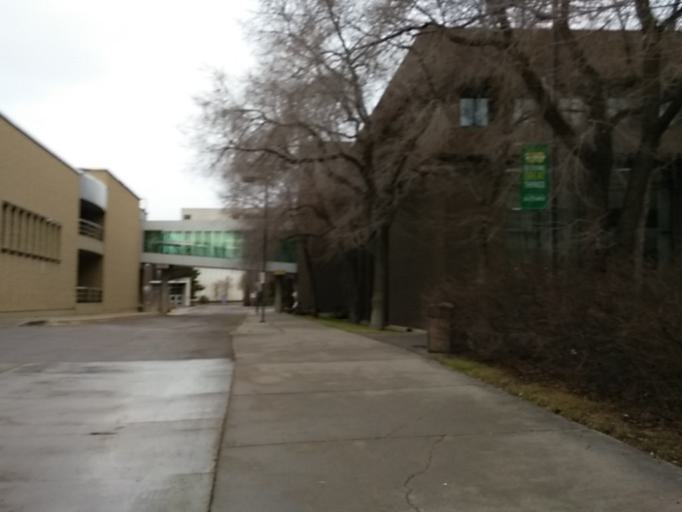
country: CA
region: Alberta
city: Edmonton
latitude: 53.5239
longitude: -113.5191
